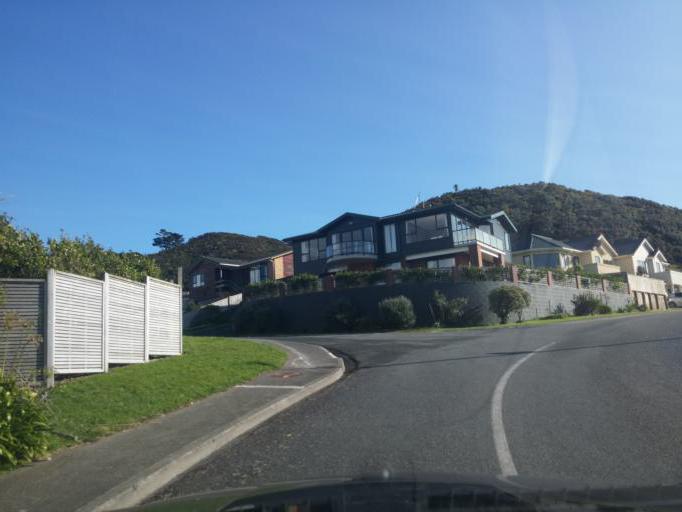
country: NZ
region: Wellington
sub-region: Wellington City
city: Wellington
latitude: -41.2360
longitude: 174.7926
